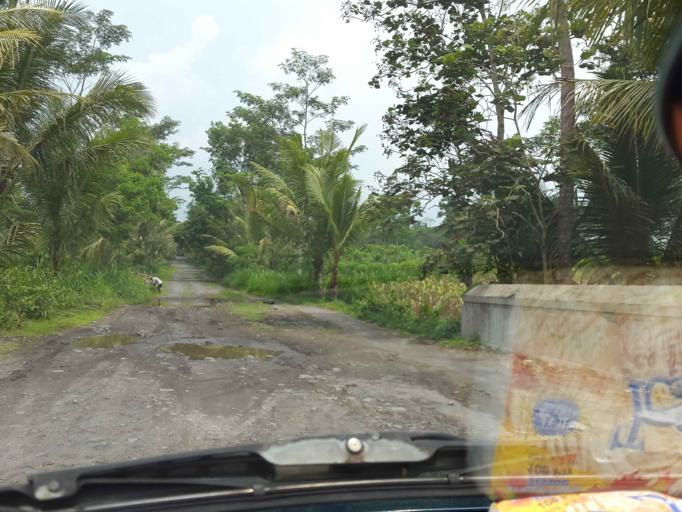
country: ID
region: Central Java
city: Muntilan
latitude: -7.5979
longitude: 110.3145
